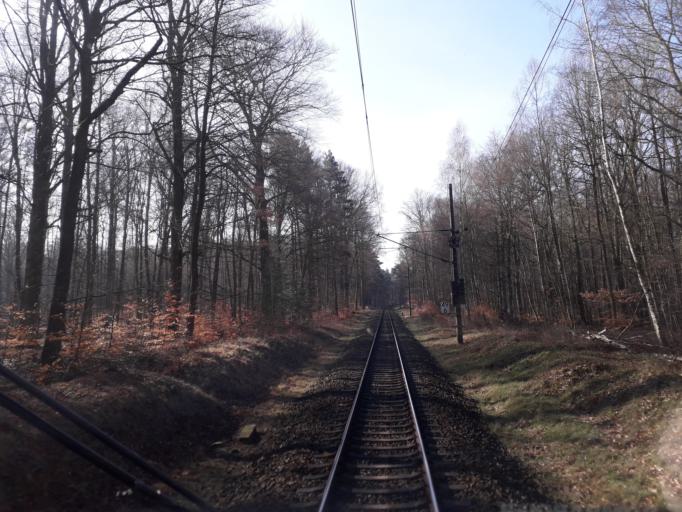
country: DE
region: Brandenburg
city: Michendorf
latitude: 52.3222
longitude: 12.9726
